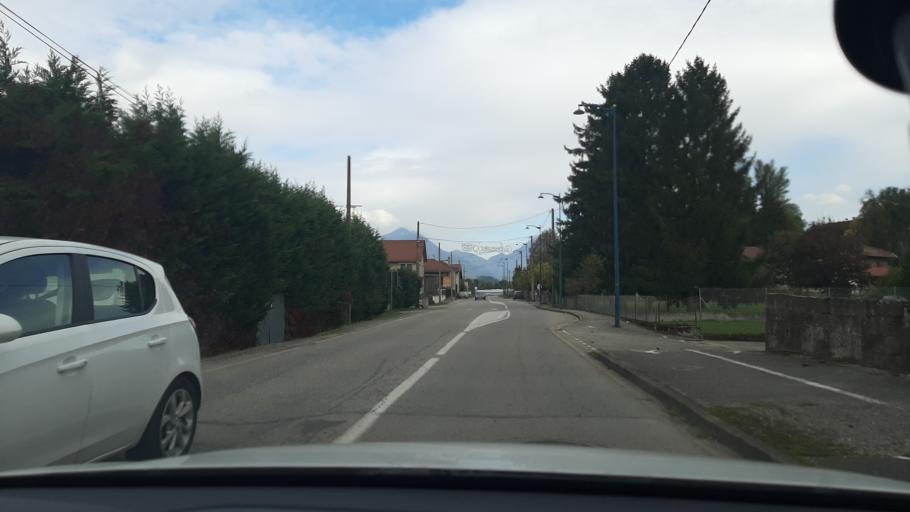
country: FR
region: Rhone-Alpes
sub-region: Departement de l'Isere
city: Pontcharra
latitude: 45.4400
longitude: 6.0295
